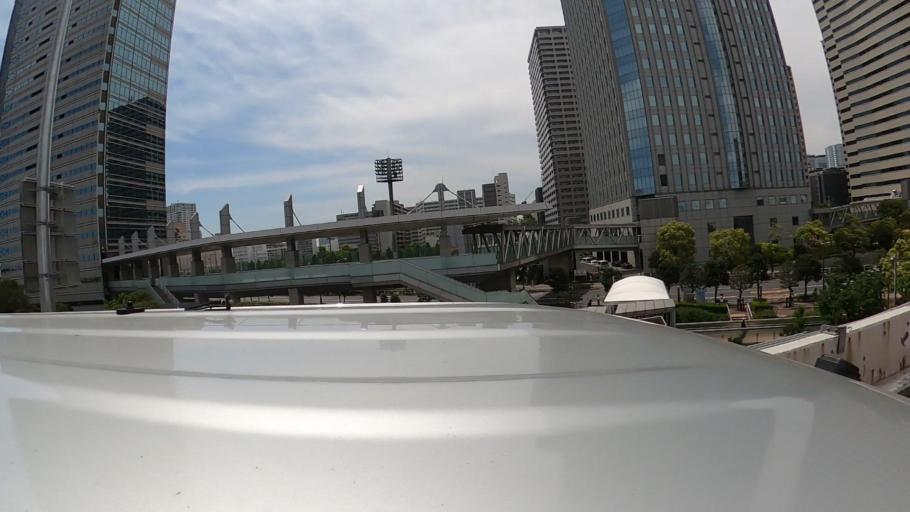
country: JP
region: Tokyo
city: Tokyo
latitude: 35.6211
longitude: 139.7513
